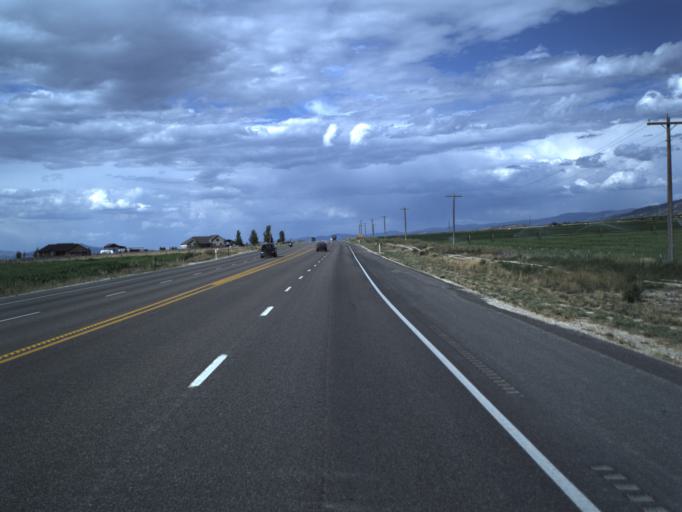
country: US
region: Utah
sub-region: Sanpete County
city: Manti
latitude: 39.3022
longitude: -111.6172
